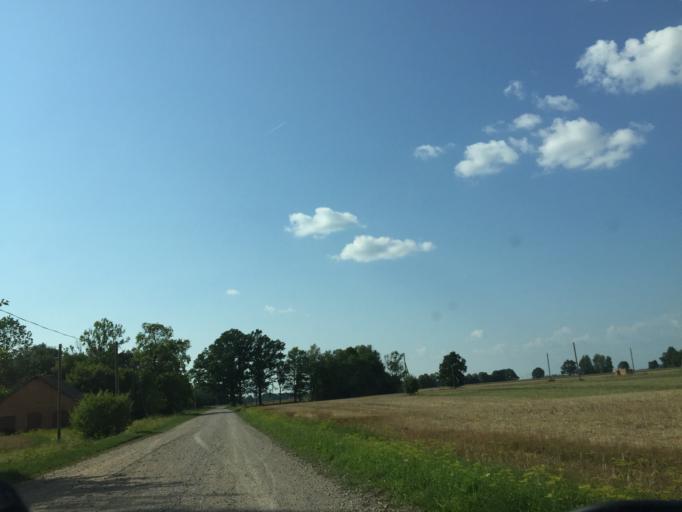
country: LV
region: Jelgava
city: Jelgava
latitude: 56.4520
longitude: 23.7409
